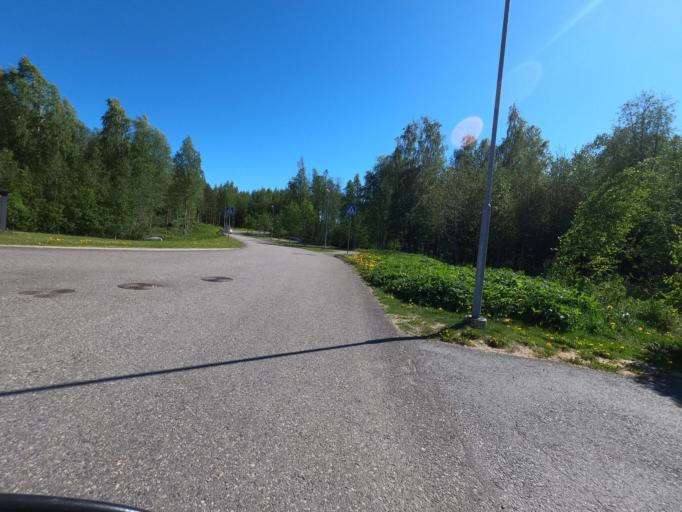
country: FI
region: North Karelia
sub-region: Joensuu
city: Joensuu
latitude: 62.6032
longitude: 29.8250
